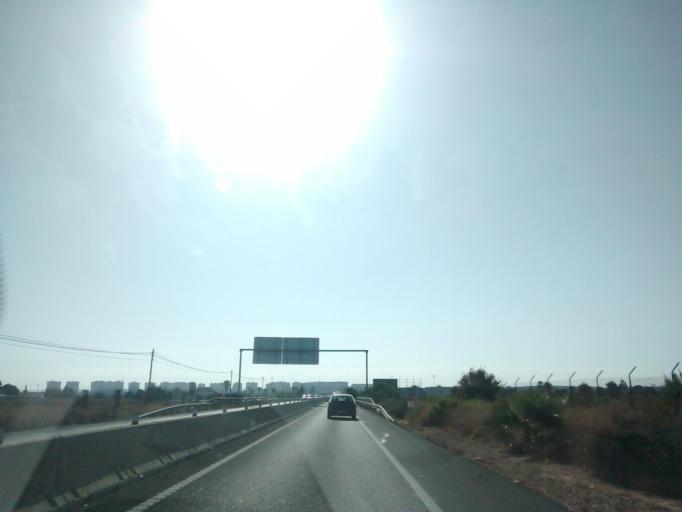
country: ES
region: Valencia
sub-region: Provincia de Alicante
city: Alicante
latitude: 38.2875
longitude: -0.5465
